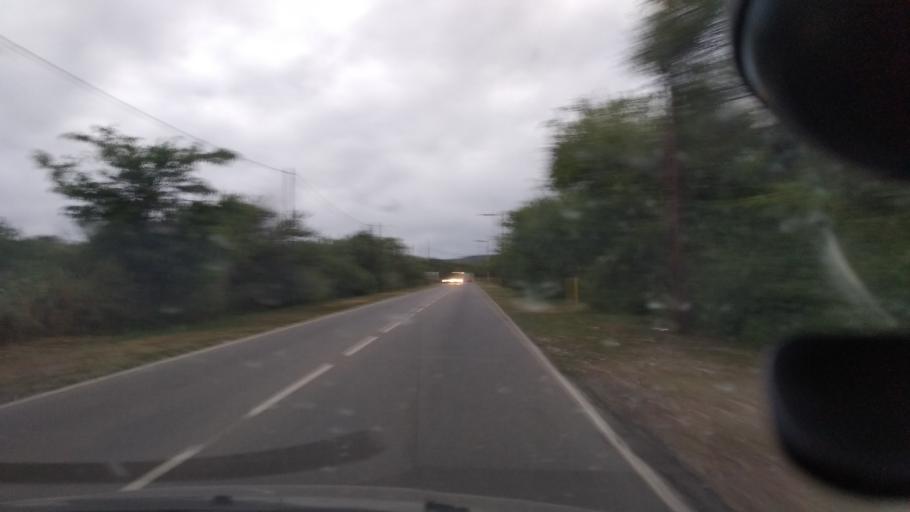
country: AR
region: Cordoba
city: Villa Las Rosas
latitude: -31.9330
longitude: -65.0393
